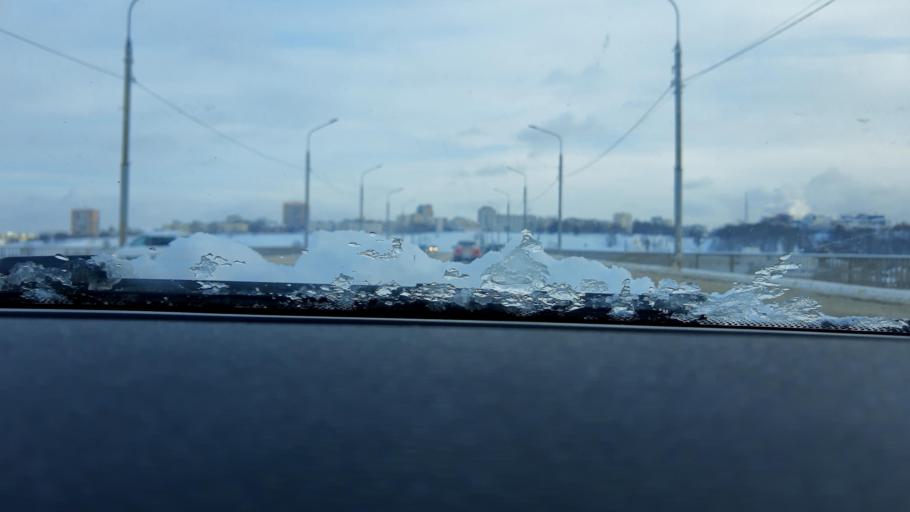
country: RU
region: Nizjnij Novgorod
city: Nizhniy Novgorod
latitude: 56.3317
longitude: 43.9774
